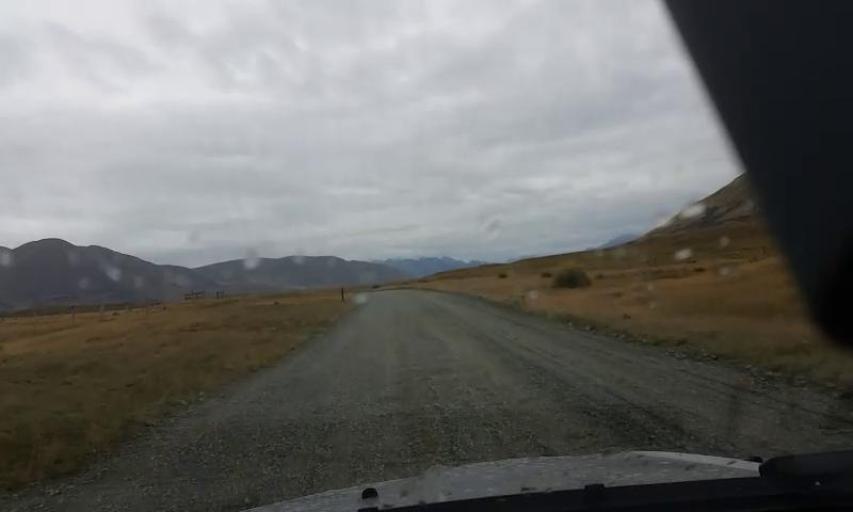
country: NZ
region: Canterbury
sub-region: Ashburton District
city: Methven
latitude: -43.6151
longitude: 171.1060
